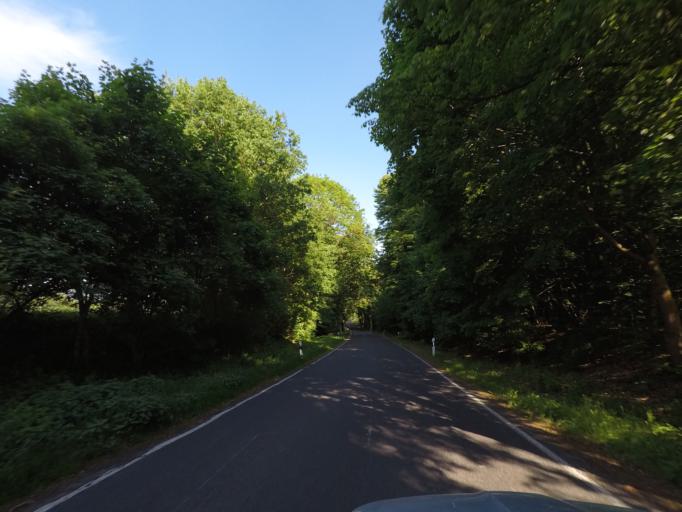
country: DE
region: Brandenburg
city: Hohenfinow
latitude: 52.7242
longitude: 13.8859
